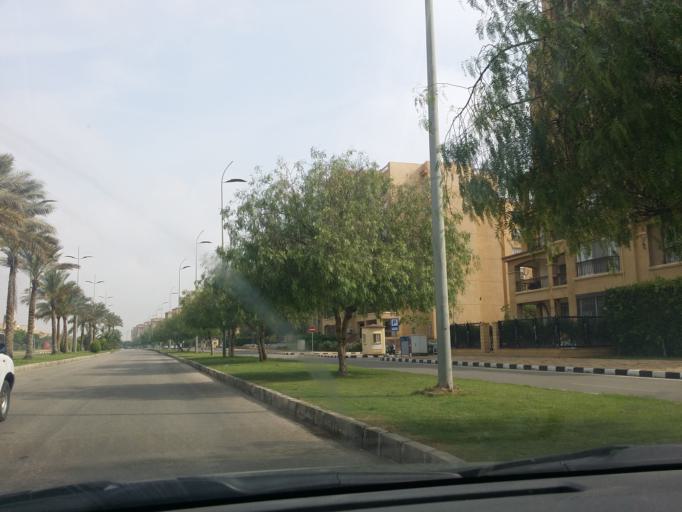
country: EG
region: Muhafazat al Qalyubiyah
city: Al Khankah
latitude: 30.0975
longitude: 31.6345
